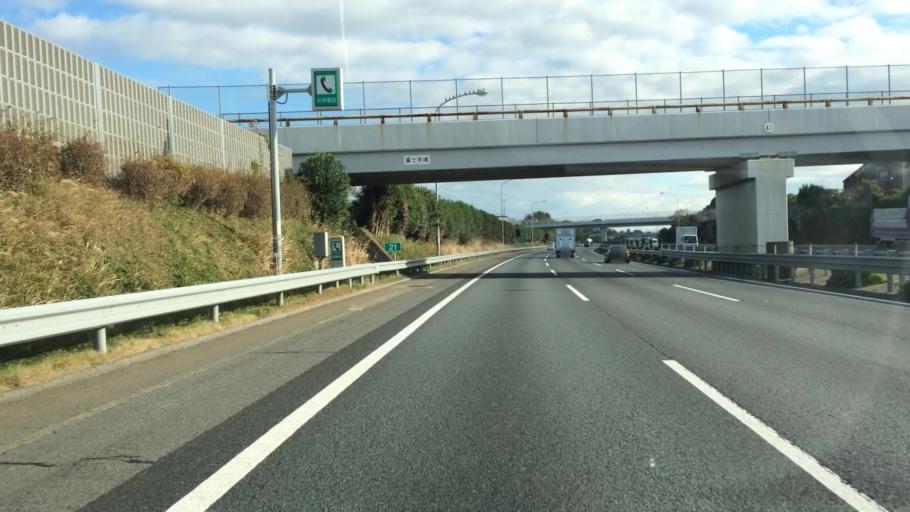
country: JP
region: Chiba
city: Yotsukaido
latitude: 35.6796
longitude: 140.1395
